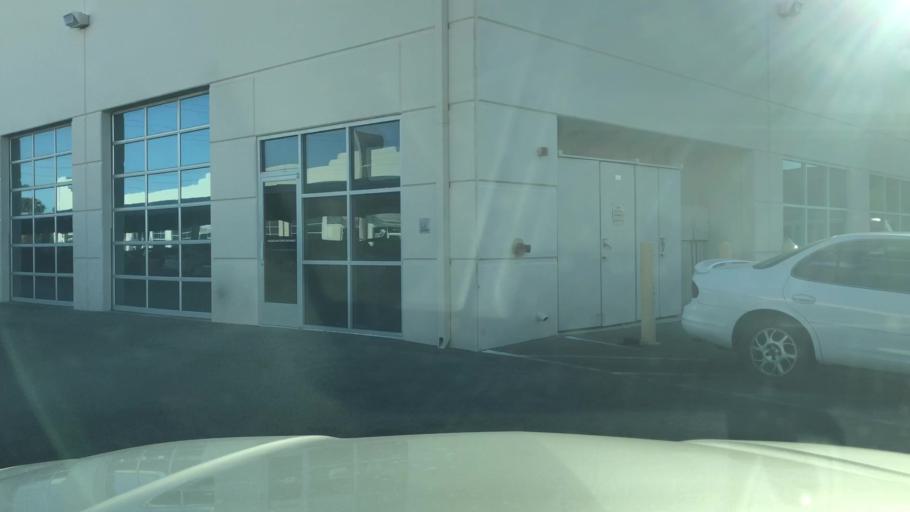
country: US
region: Nevada
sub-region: Clark County
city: Whitney
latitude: 36.0405
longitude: -115.0405
